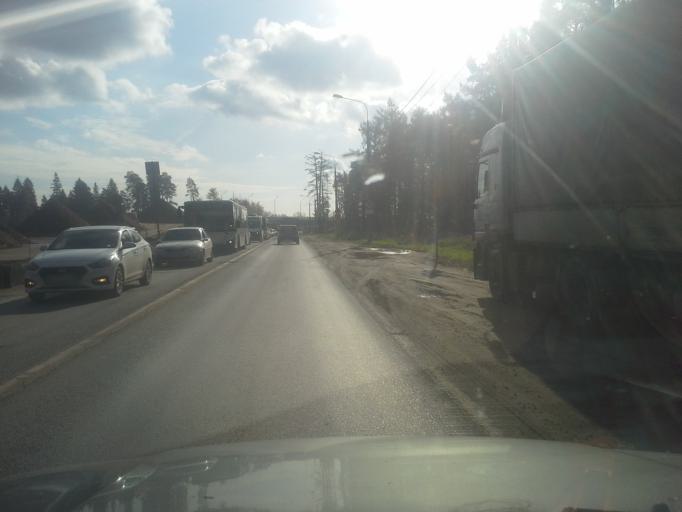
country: RU
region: Moskovskaya
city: Zvenigorod
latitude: 55.7037
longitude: 36.8790
